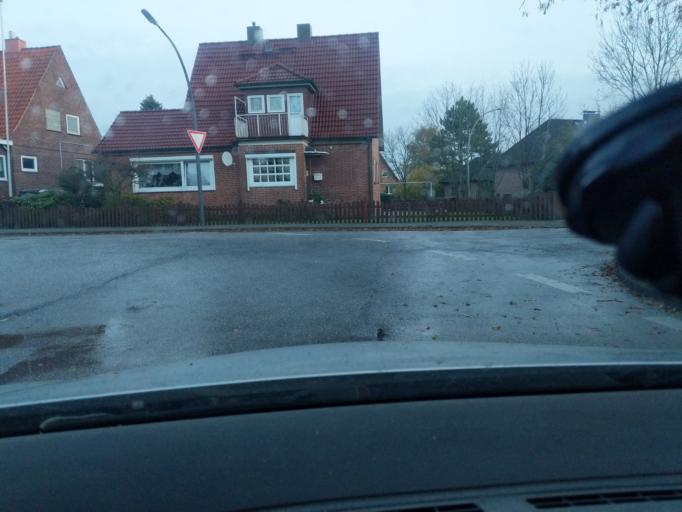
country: DE
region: Lower Saxony
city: Neu Wulmstorf
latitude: 53.5184
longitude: 9.7815
